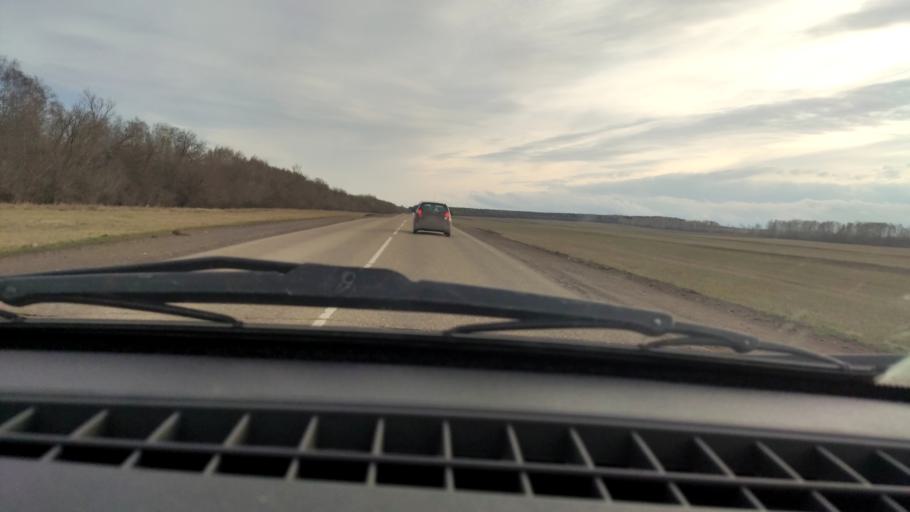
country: RU
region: Bashkortostan
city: Davlekanovo
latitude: 54.2582
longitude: 55.0876
